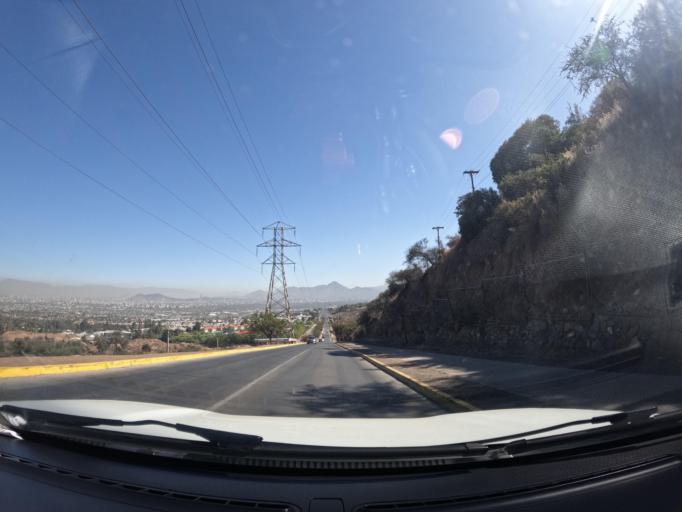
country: CL
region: Santiago Metropolitan
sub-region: Provincia de Santiago
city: Villa Presidente Frei, Nunoa, Santiago, Chile
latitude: -33.4884
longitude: -70.5200
